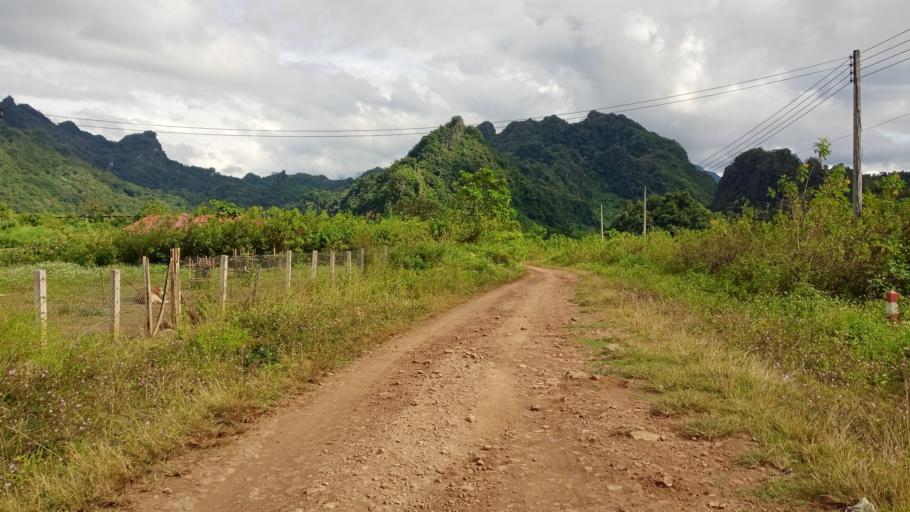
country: LA
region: Xiangkhoang
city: Phonsavan
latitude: 19.1051
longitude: 102.9307
